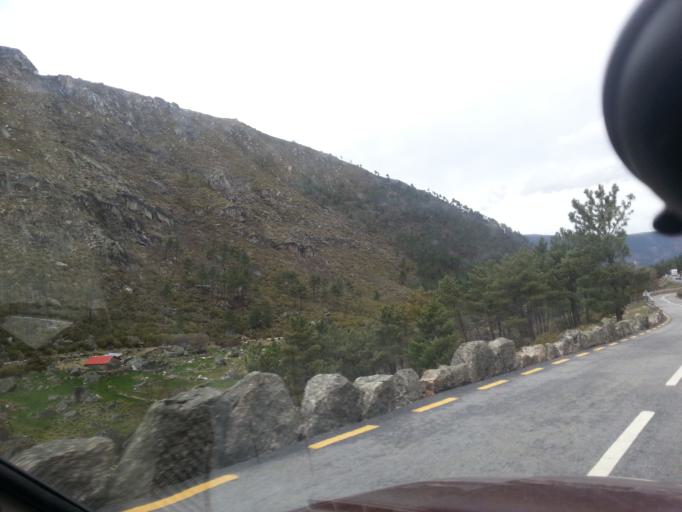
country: PT
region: Guarda
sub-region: Manteigas
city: Manteigas
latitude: 40.3591
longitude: -7.5557
